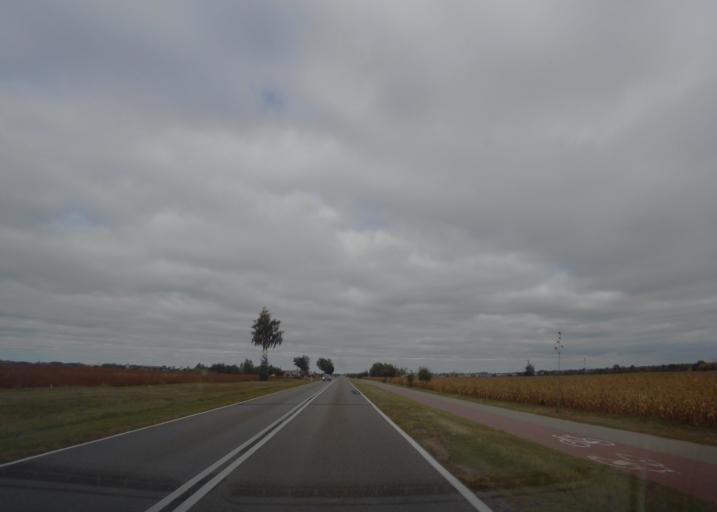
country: PL
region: Lublin Voivodeship
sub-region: Powiat wlodawski
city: Wlodawa
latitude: 51.5287
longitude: 23.5244
